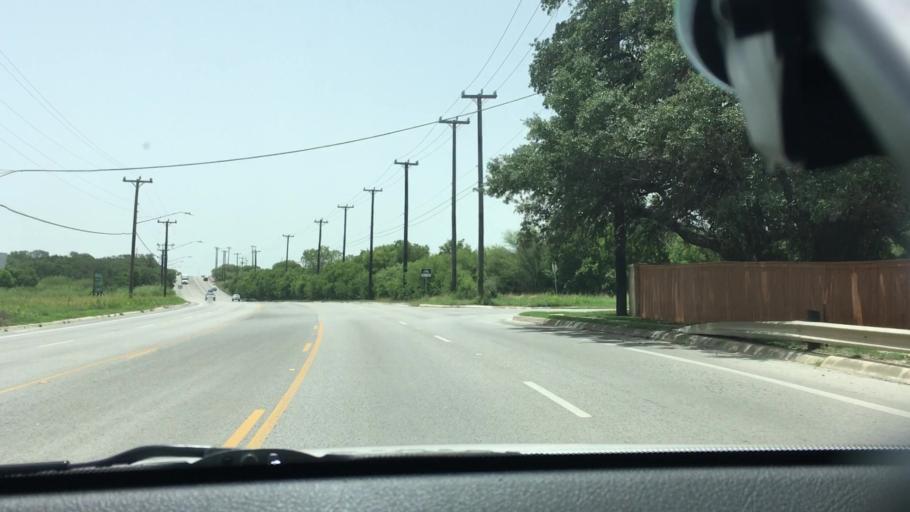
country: US
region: Texas
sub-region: Bexar County
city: Live Oak
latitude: 29.5613
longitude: -98.3520
